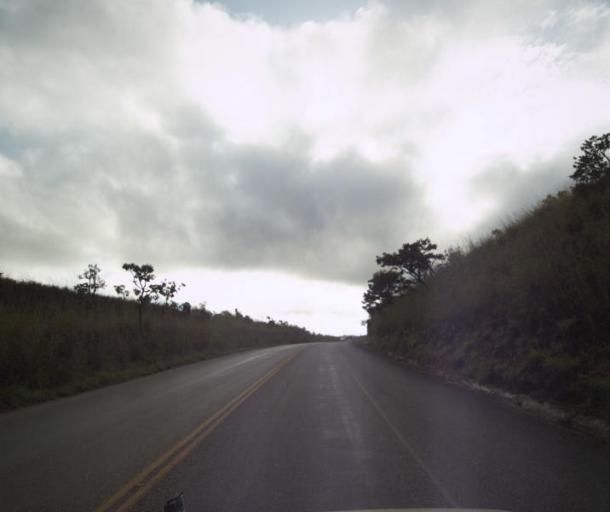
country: BR
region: Goias
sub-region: Pirenopolis
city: Pirenopolis
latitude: -15.7240
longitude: -48.7041
